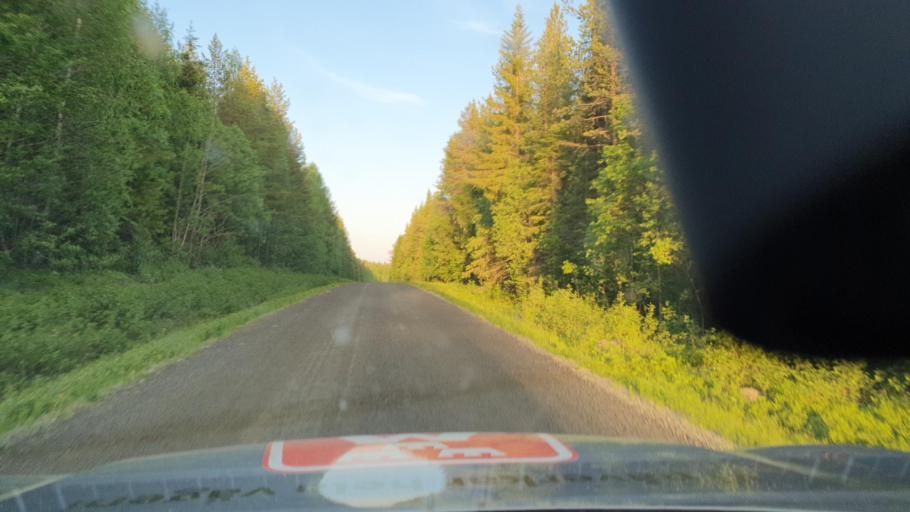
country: SE
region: Norrbotten
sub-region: Bodens Kommun
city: Boden
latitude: 66.0645
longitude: 21.7240
